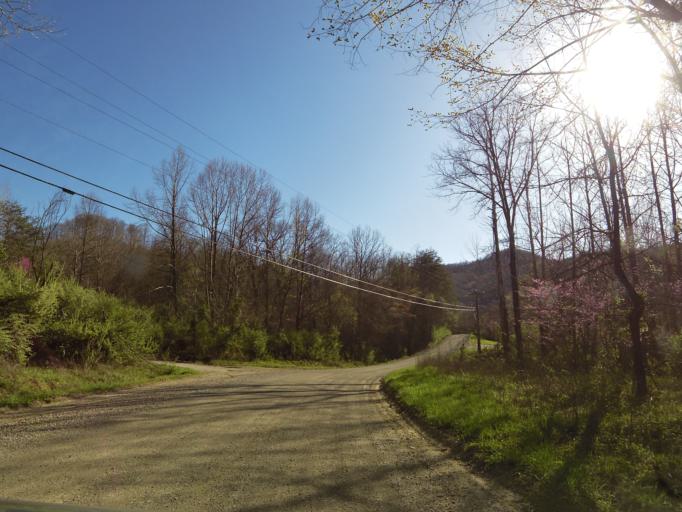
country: US
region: Tennessee
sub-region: Scott County
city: Huntsville
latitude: 36.3058
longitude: -84.3825
